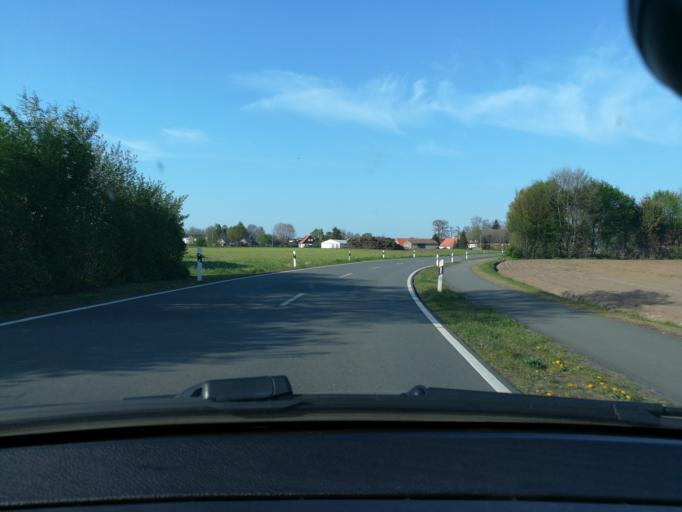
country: DE
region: North Rhine-Westphalia
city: Versmold
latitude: 52.0284
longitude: 8.1428
